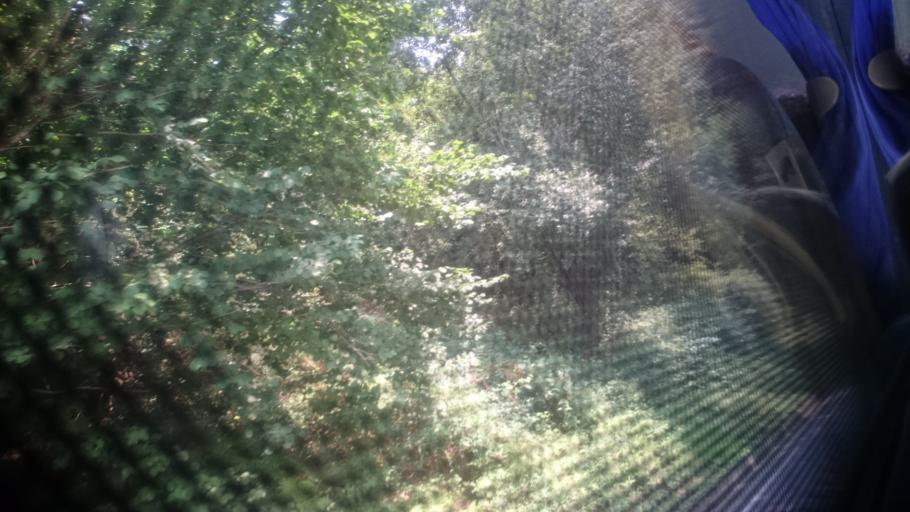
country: ES
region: Asturias
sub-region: Province of Asturias
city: Amieva
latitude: 43.3035
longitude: -5.0429
